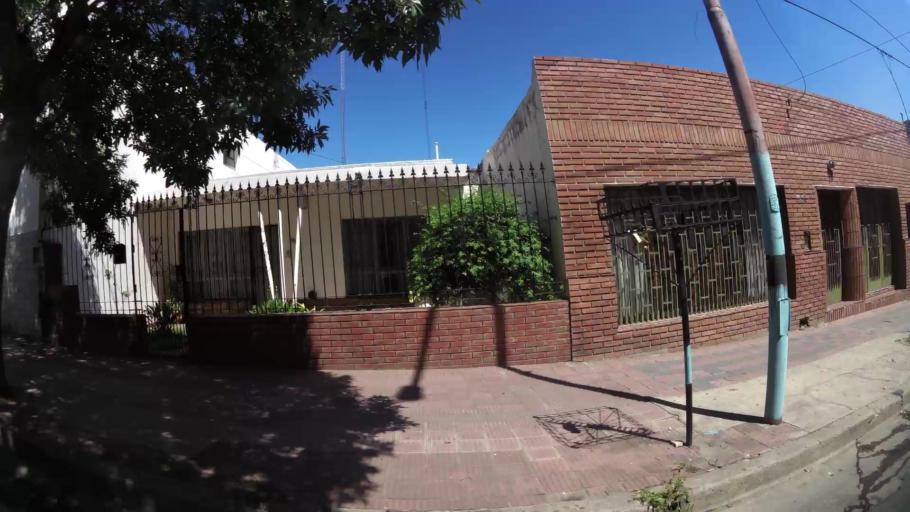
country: AR
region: Cordoba
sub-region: Departamento de Capital
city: Cordoba
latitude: -31.4260
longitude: -64.1510
